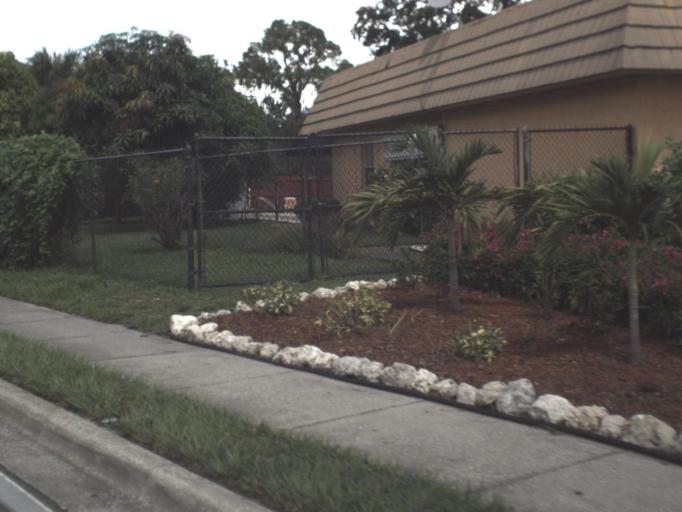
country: US
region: Florida
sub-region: Manatee County
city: Whitfield
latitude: 27.3801
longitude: -82.5561
